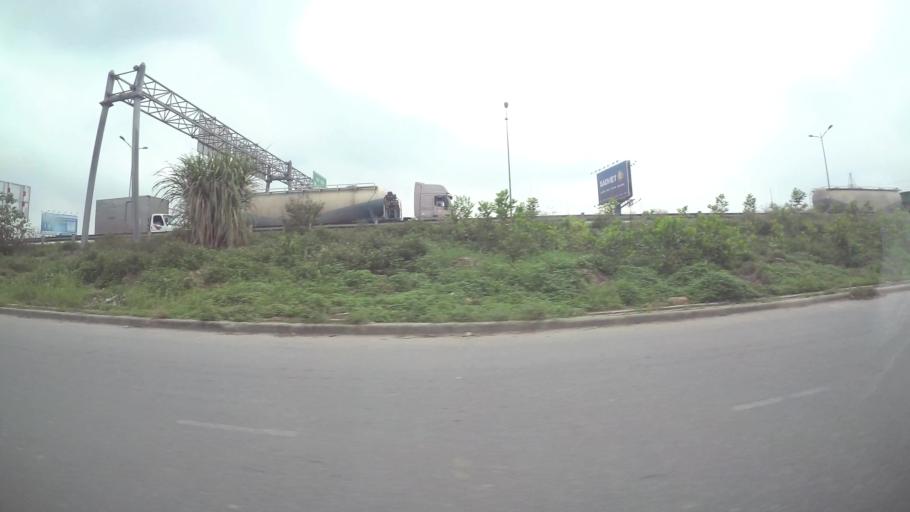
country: VN
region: Ha Noi
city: Trau Quy
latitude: 21.0315
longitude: 105.9318
